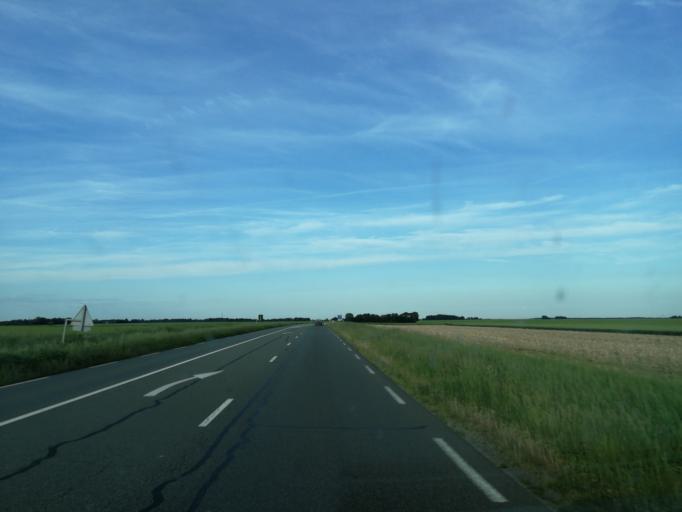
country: FR
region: Centre
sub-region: Departement d'Eure-et-Loir
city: Gallardon
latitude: 48.5019
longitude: 1.7322
